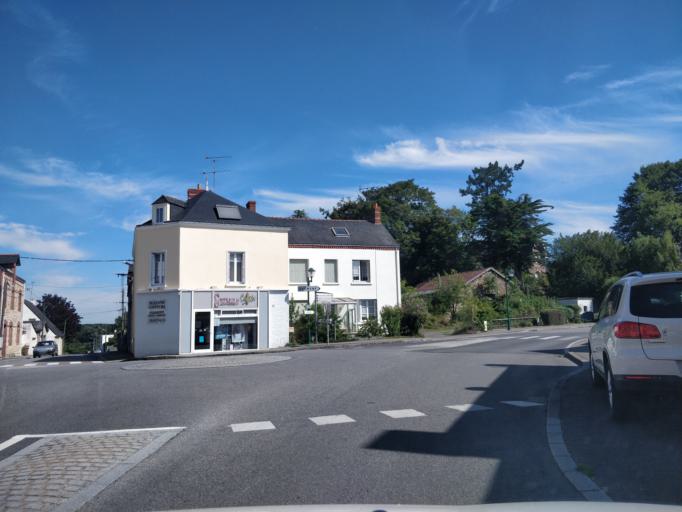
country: FR
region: Pays de la Loire
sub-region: Departement de la Loire-Atlantique
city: Plesse
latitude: 47.5427
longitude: -1.8870
